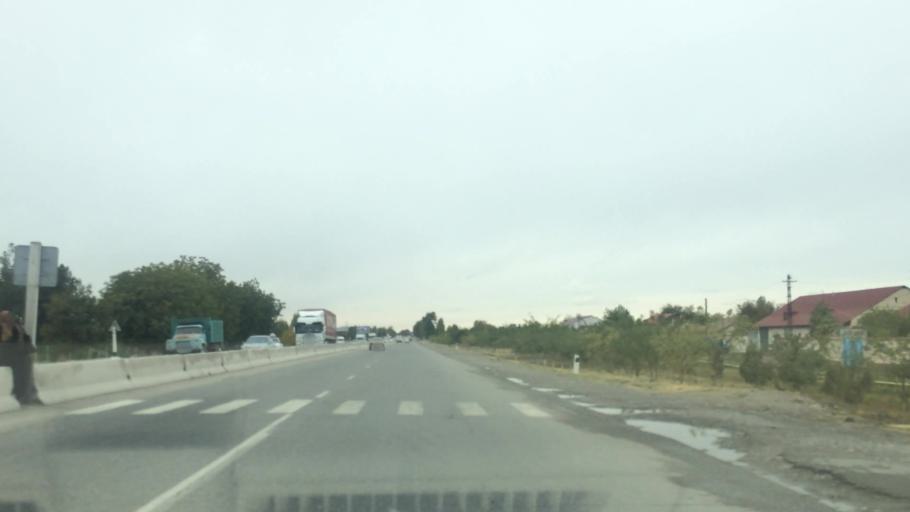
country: UZ
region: Samarqand
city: Jomboy
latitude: 39.7248
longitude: 67.1344
